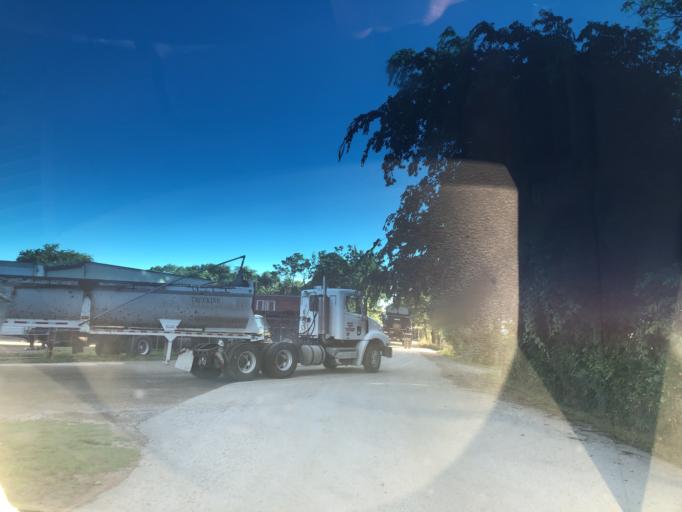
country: US
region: Texas
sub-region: Dallas County
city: Grand Prairie
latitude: 32.7891
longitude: -97.0091
